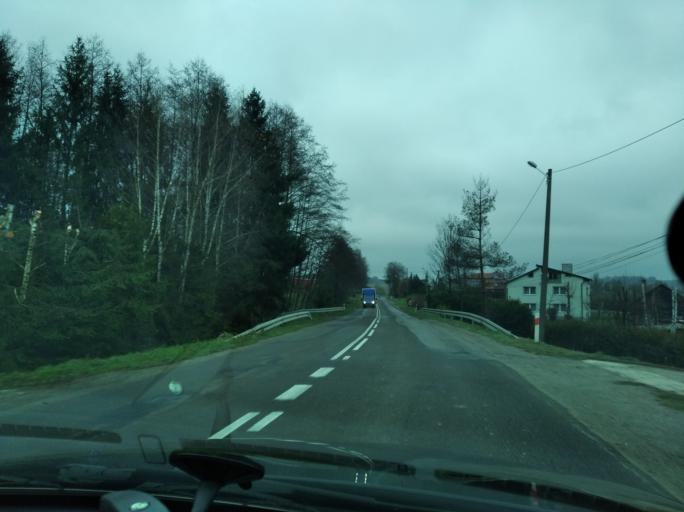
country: PL
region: Subcarpathian Voivodeship
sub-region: Powiat przeworski
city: Jawornik Polski
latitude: 49.8652
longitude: 22.2472
